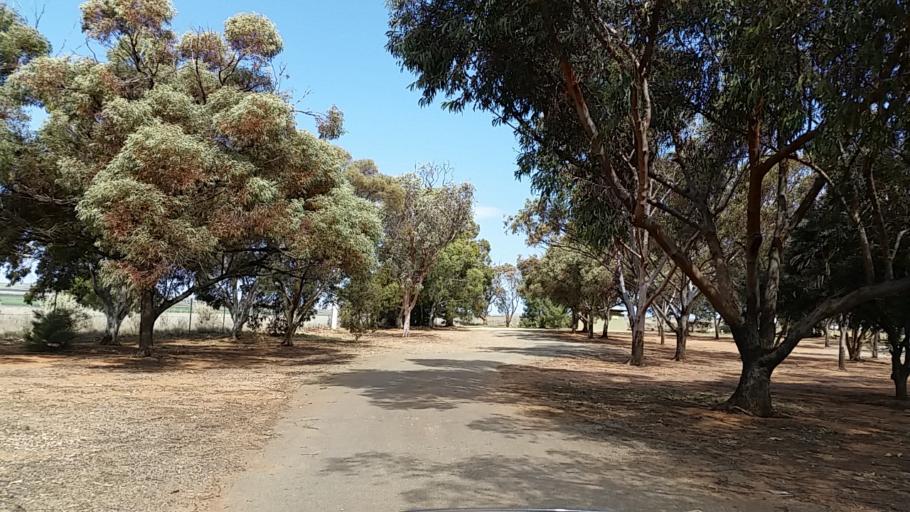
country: AU
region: South Australia
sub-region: Peterborough
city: Peterborough
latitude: -32.9798
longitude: 138.8350
